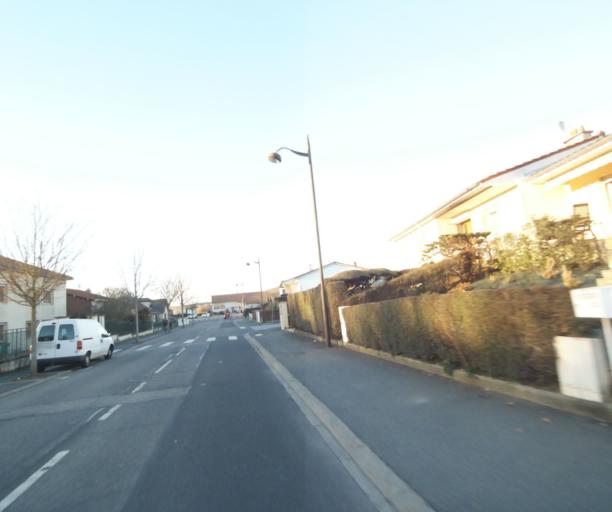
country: FR
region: Lorraine
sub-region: Departement de Meurthe-et-Moselle
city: Pulnoy
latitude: 48.7040
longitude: 6.2575
